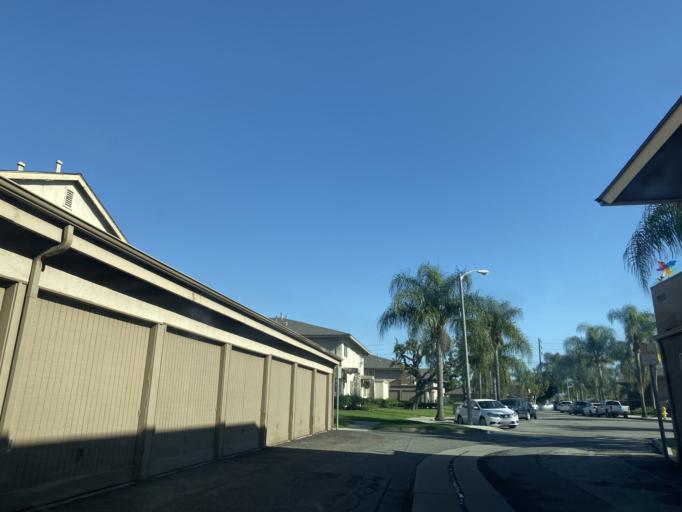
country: US
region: California
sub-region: Orange County
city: Placentia
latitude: 33.8807
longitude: -117.8792
